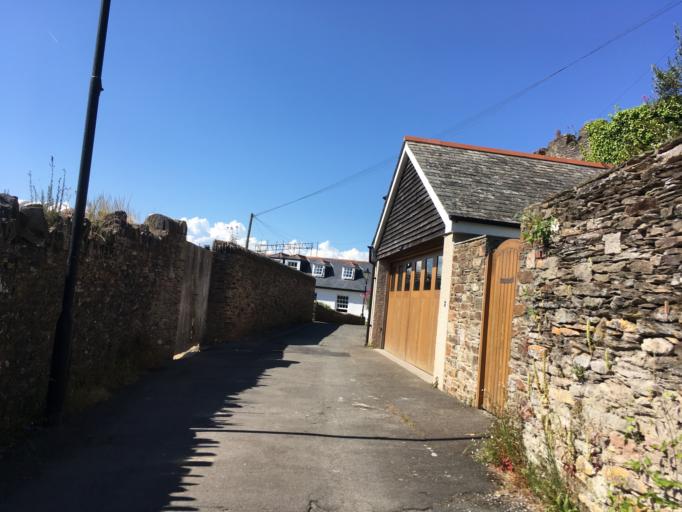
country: GB
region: England
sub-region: Devon
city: Dartmouth
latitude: 50.3477
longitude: -3.5724
